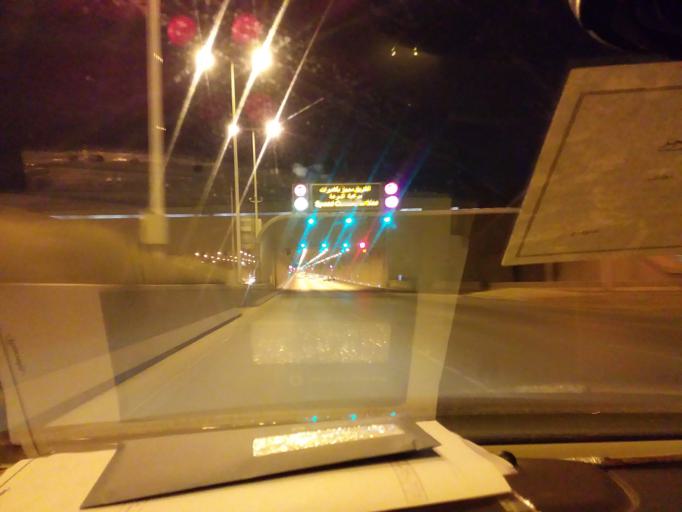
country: SA
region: Ar Riyad
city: Riyadh
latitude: 24.7274
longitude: 46.7113
